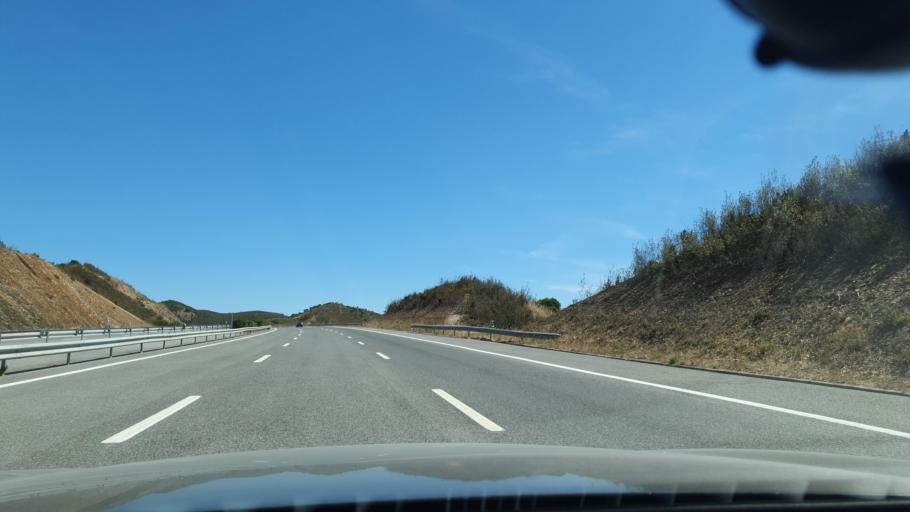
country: PT
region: Faro
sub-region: Silves
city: Sao Bartolomeu de Messines
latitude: 37.3430
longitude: -8.2596
